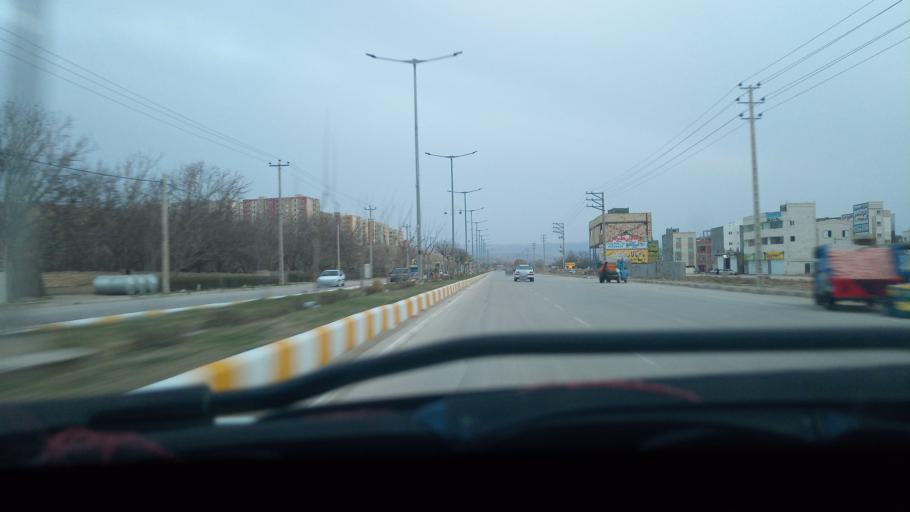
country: IR
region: Khorasan-e Shomali
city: Bojnurd
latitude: 37.4539
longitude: 57.3179
